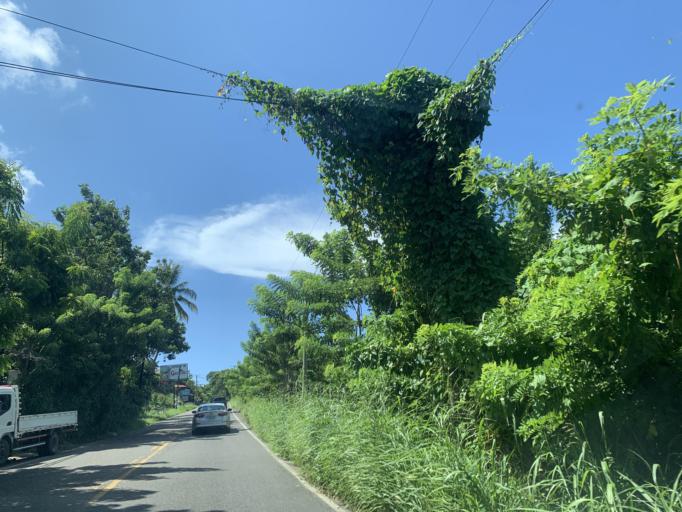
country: DO
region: Maria Trinidad Sanchez
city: Cabrera
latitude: 19.6489
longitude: -69.9282
